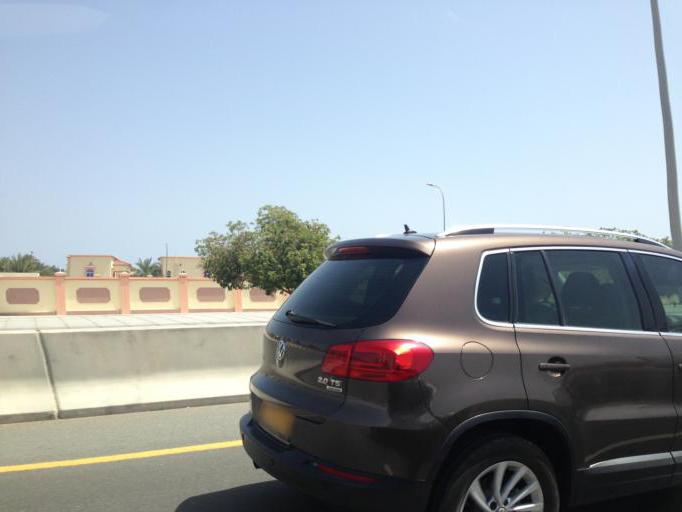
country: OM
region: Muhafazat Masqat
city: Bawshar
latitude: 23.6036
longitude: 58.3352
